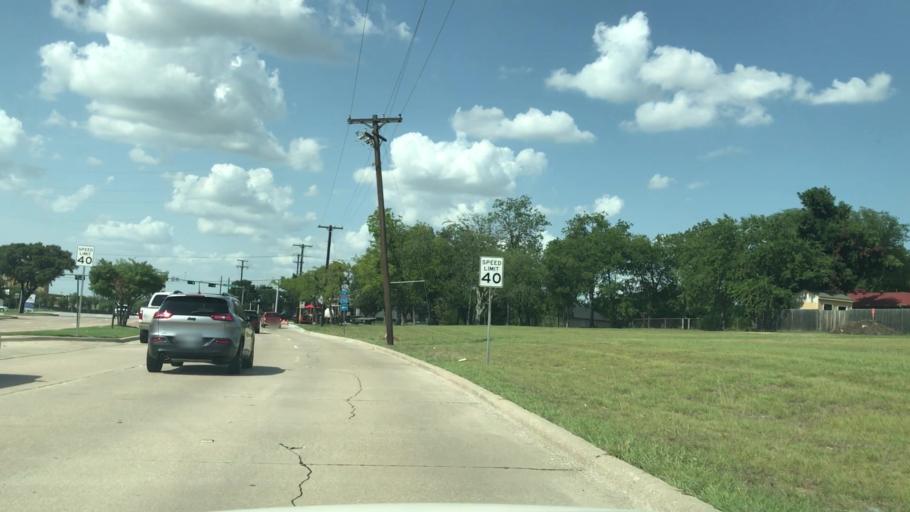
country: US
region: Texas
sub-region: Dallas County
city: Carrollton
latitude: 32.9671
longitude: -96.9118
